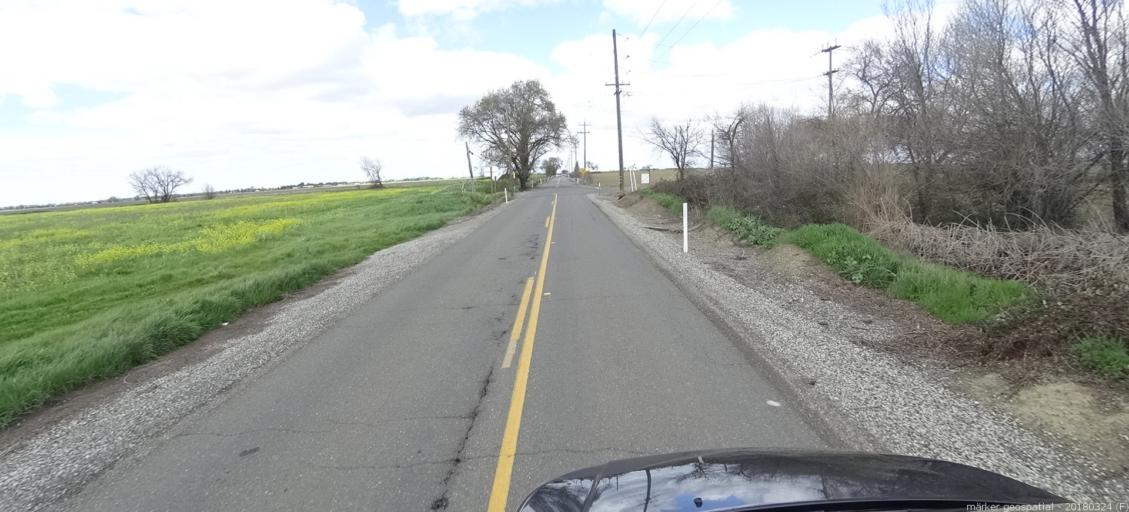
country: US
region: California
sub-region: Yolo County
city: West Sacramento
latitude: 38.6557
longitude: -121.5766
